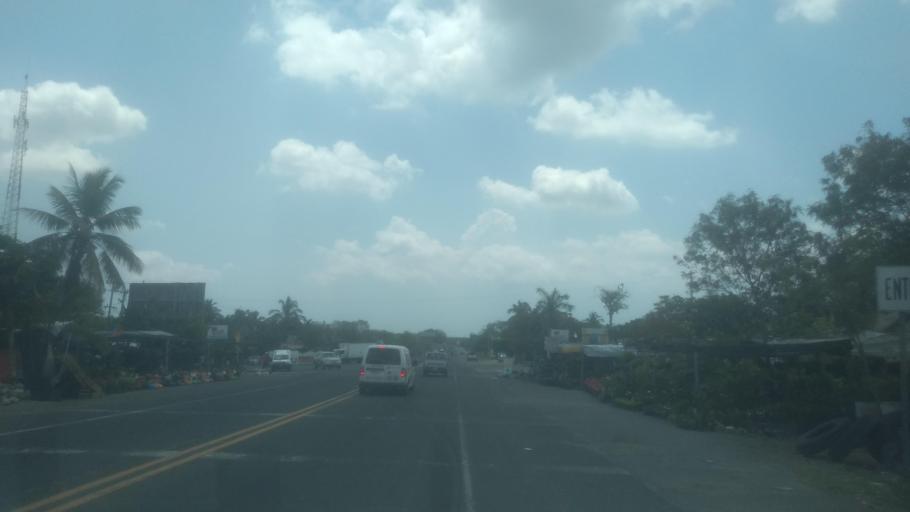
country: MX
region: Veracruz
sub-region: Emiliano Zapata
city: Plan del Rio
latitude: 19.3933
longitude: -96.6202
